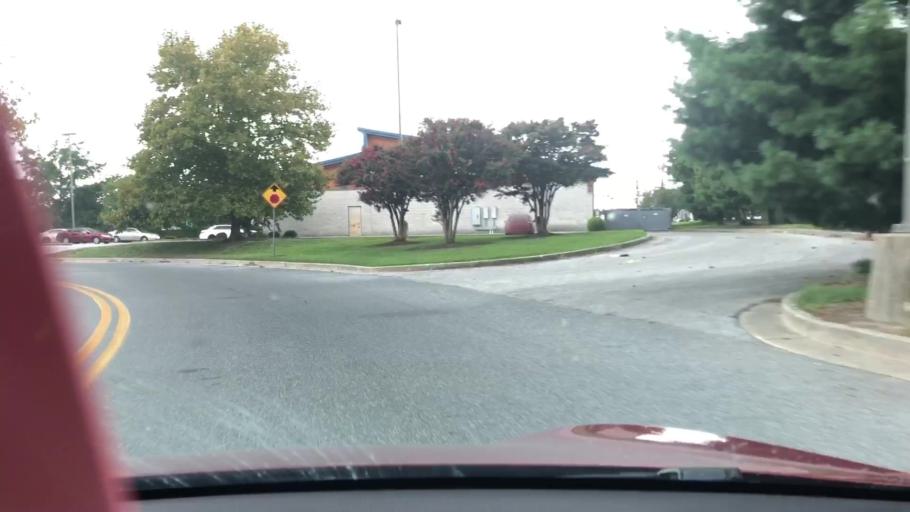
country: US
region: Maryland
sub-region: Wicomico County
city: Salisbury
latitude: 38.4021
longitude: -75.5676
